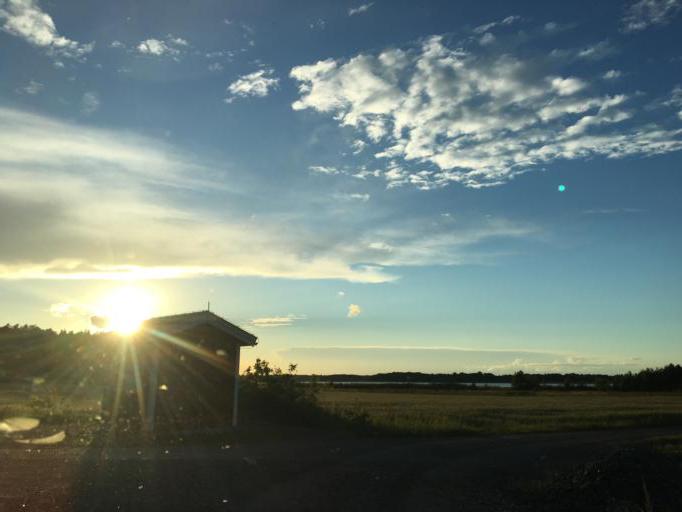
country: SE
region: Soedermanland
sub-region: Eskilstuna Kommun
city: Torshalla
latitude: 59.4330
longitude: 16.4345
